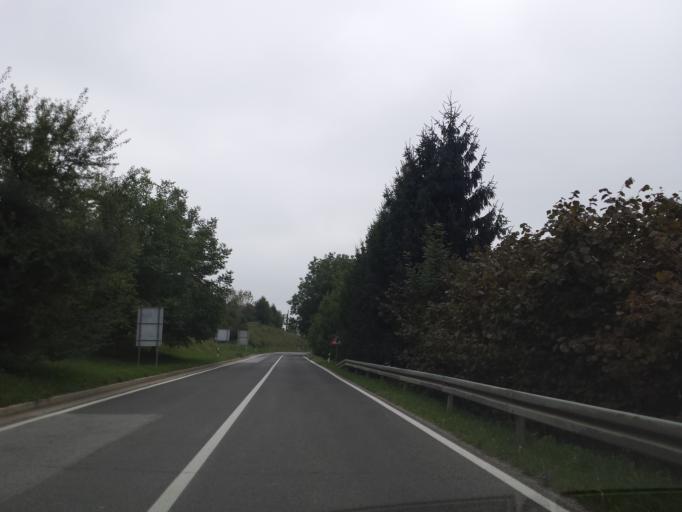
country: HR
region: Karlovacka
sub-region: Grad Karlovac
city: Karlovac
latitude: 45.4512
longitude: 15.4922
